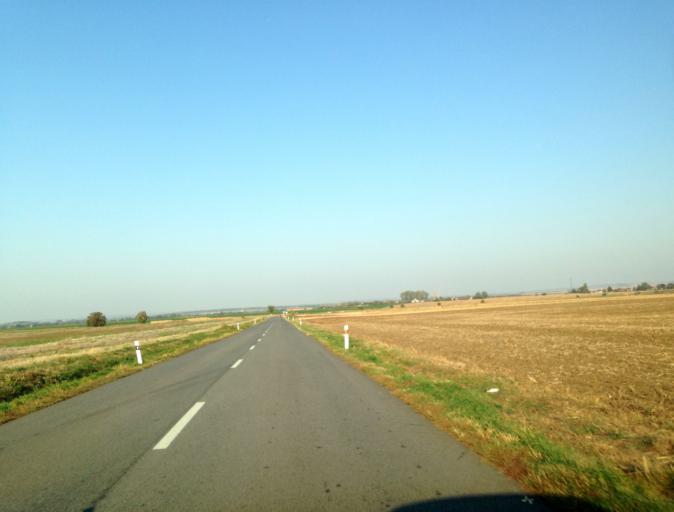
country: SK
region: Nitriansky
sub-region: Okres Komarno
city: Hurbanovo
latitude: 47.9095
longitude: 18.2879
